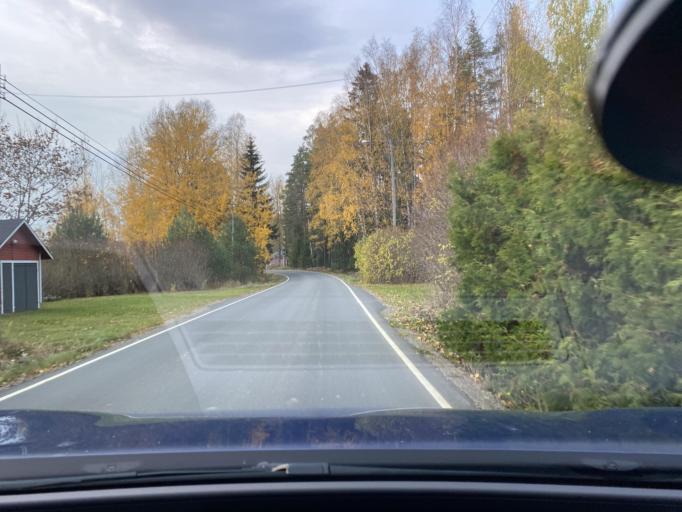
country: FI
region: Varsinais-Suomi
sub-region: Loimaa
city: Alastaro
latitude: 61.0858
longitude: 22.9168
